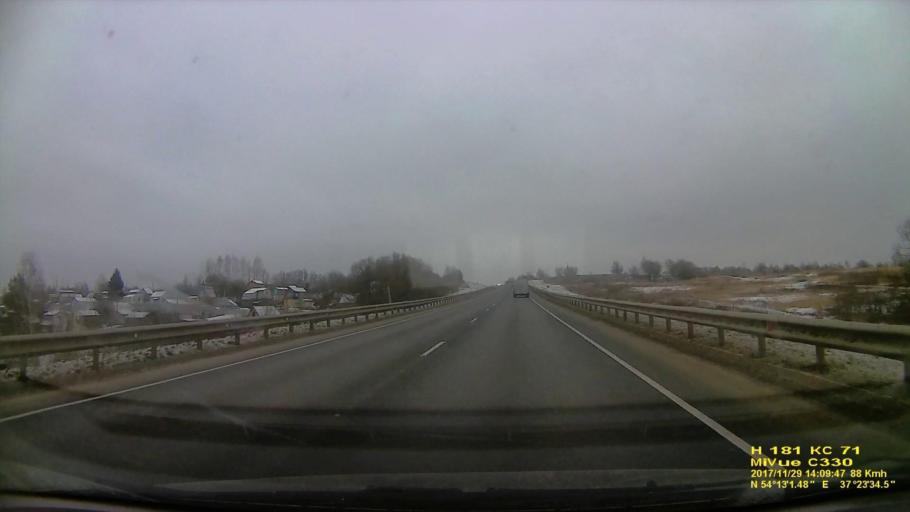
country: RU
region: Tula
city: Leninskiy
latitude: 54.2168
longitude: 37.3932
